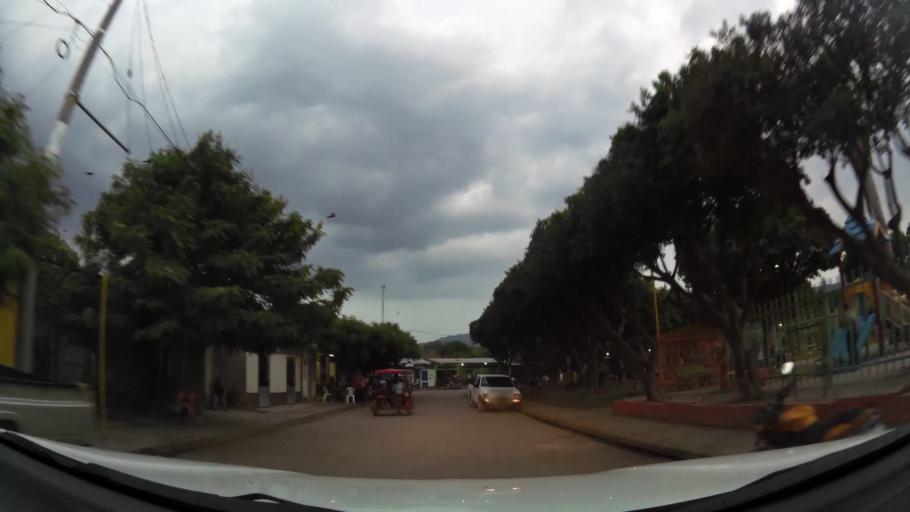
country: NI
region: Matagalpa
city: Ciudad Dario
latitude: 12.8523
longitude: -86.0956
